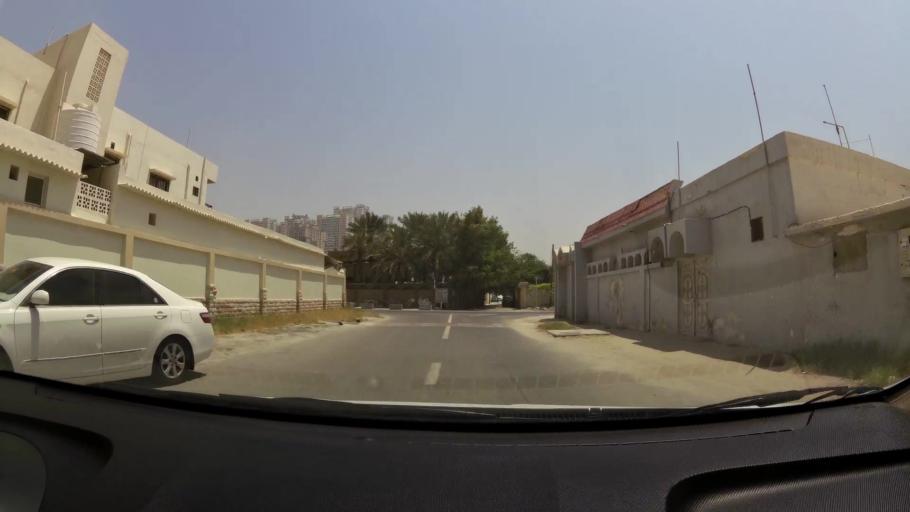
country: AE
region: Ajman
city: Ajman
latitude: 25.4022
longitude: 55.4321
